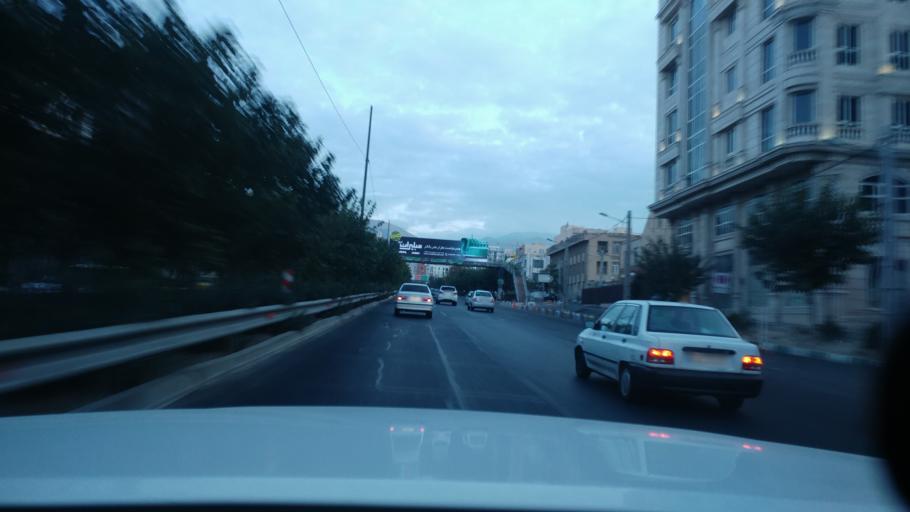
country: IR
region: Tehran
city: Tehran
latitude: 35.7375
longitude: 51.3129
